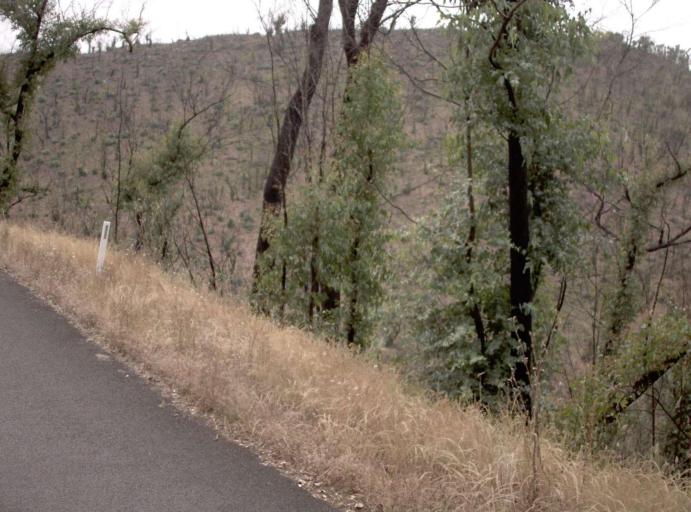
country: AU
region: Victoria
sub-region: Wellington
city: Heyfield
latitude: -37.7175
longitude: 146.6685
